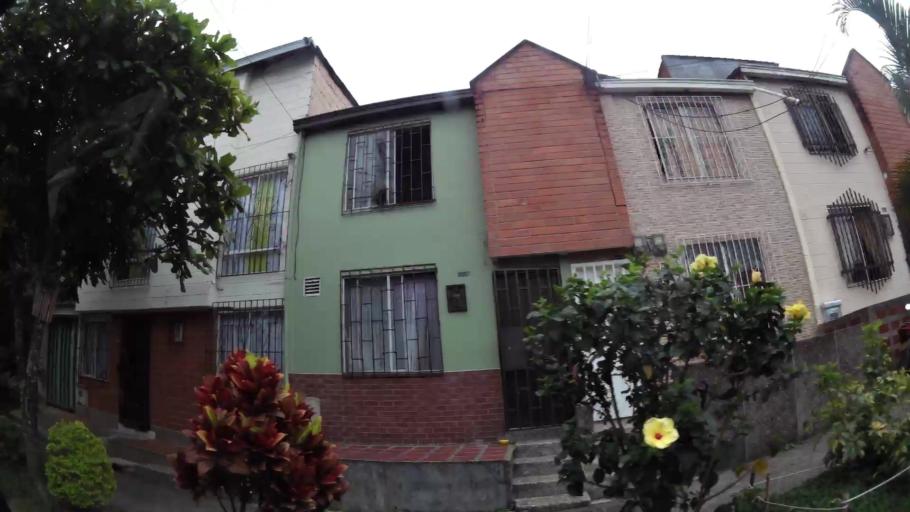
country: CO
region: Antioquia
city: Medellin
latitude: 6.2332
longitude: -75.5506
